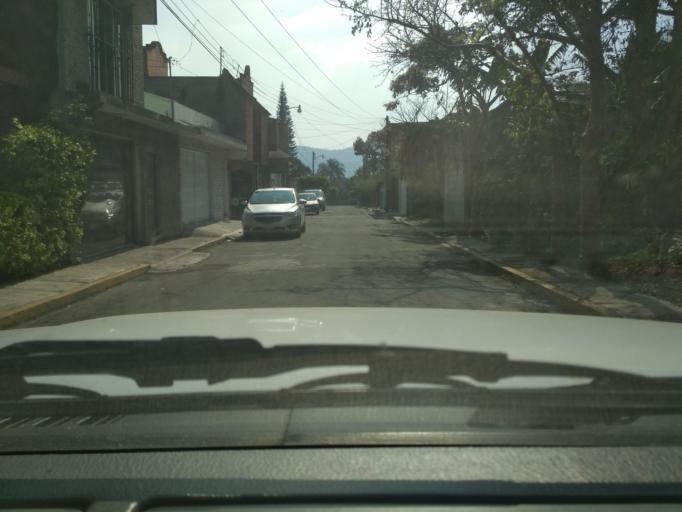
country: MX
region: Veracruz
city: Orizaba
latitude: 18.8713
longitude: -97.0923
